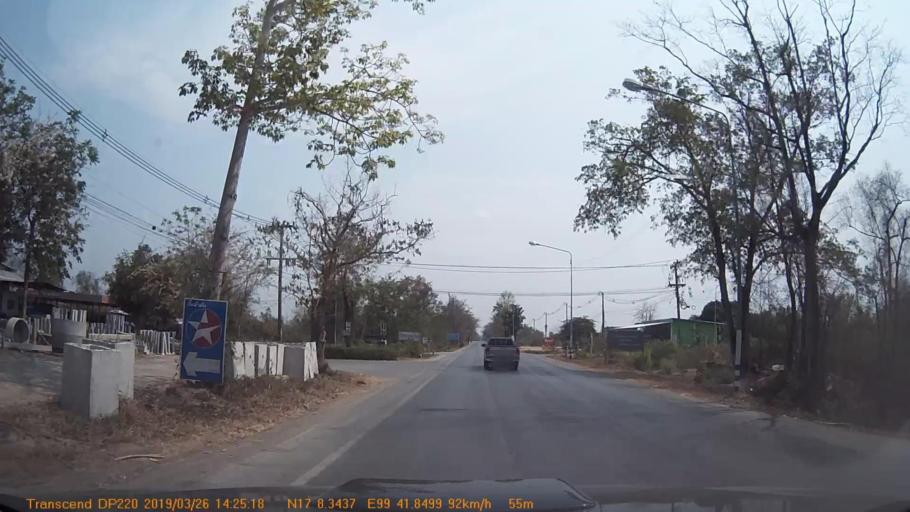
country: TH
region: Sukhothai
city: Ban Na
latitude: 17.1386
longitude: 99.6975
